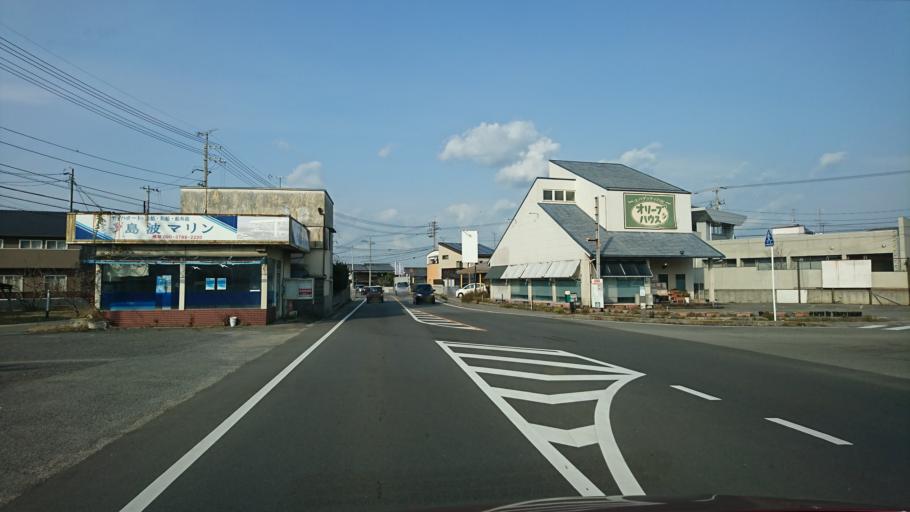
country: JP
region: Ehime
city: Saijo
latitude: 34.0259
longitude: 133.0381
